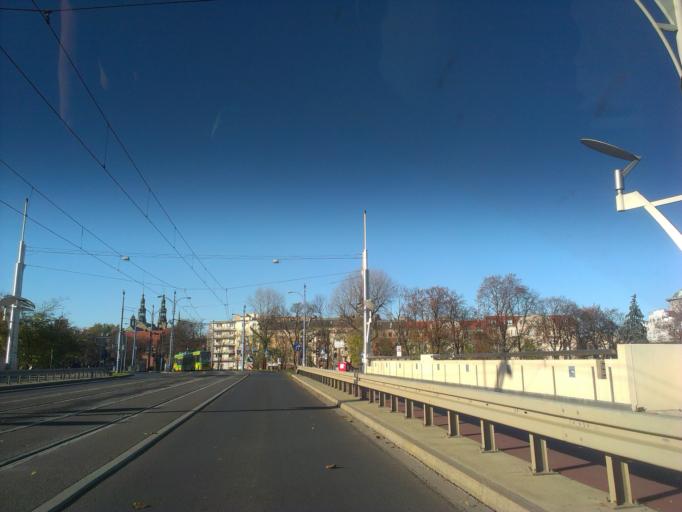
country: PL
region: Greater Poland Voivodeship
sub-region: Poznan
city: Poznan
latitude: 52.4023
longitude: 16.9440
